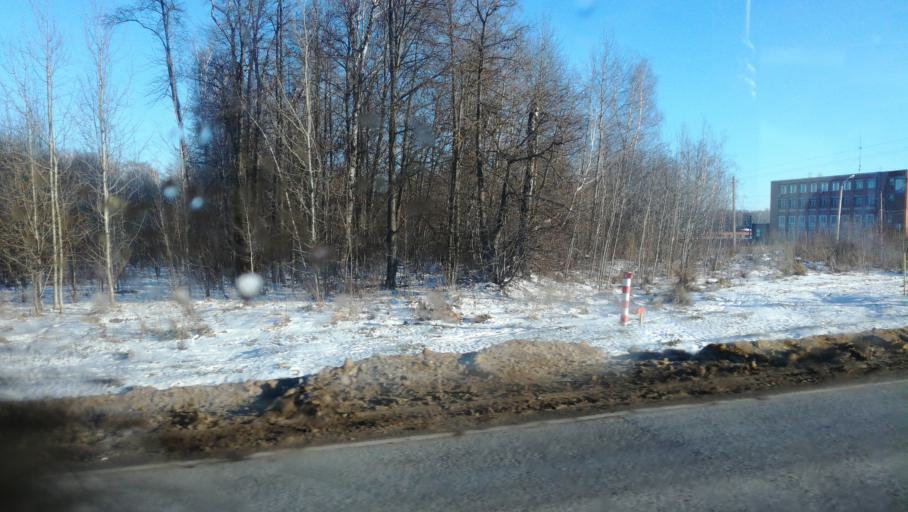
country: RU
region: Tula
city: Kosaya Gora
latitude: 54.1646
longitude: 37.4644
